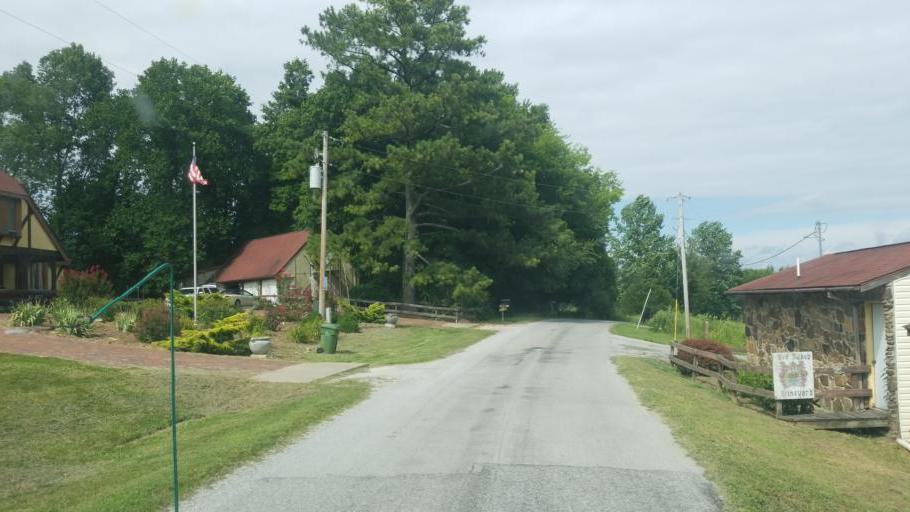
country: US
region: Illinois
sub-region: Union County
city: Cobden
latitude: 37.6129
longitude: -89.3513
